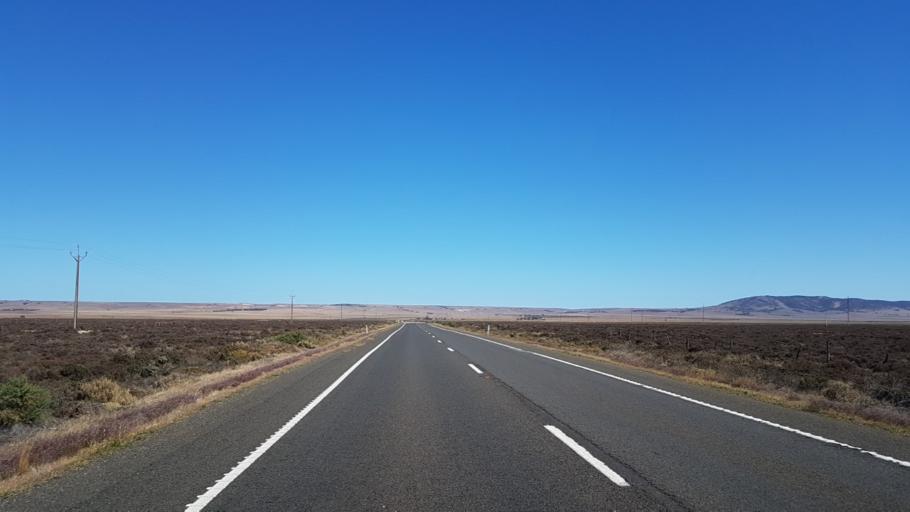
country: AU
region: South Australia
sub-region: Wakefield
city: Balaklava
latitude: -34.1060
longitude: 138.1138
